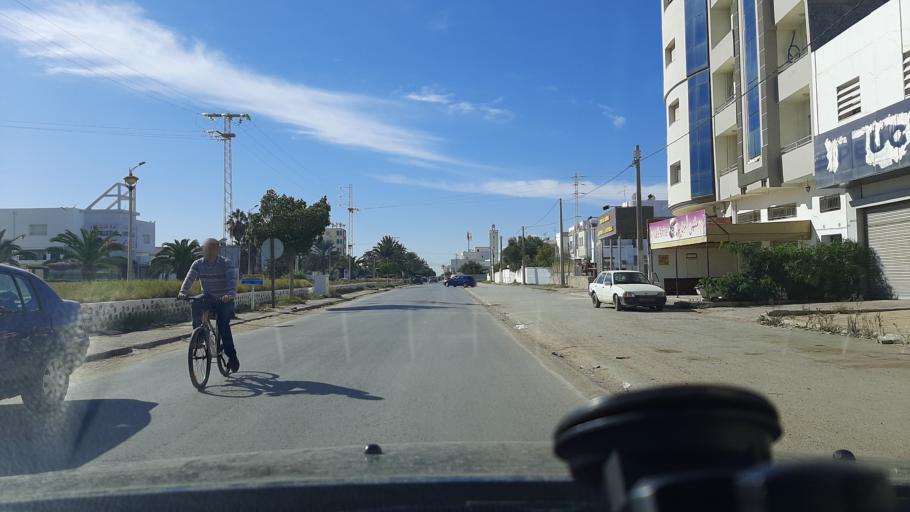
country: TN
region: Safaqis
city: Sfax
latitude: 34.7232
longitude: 10.7360
